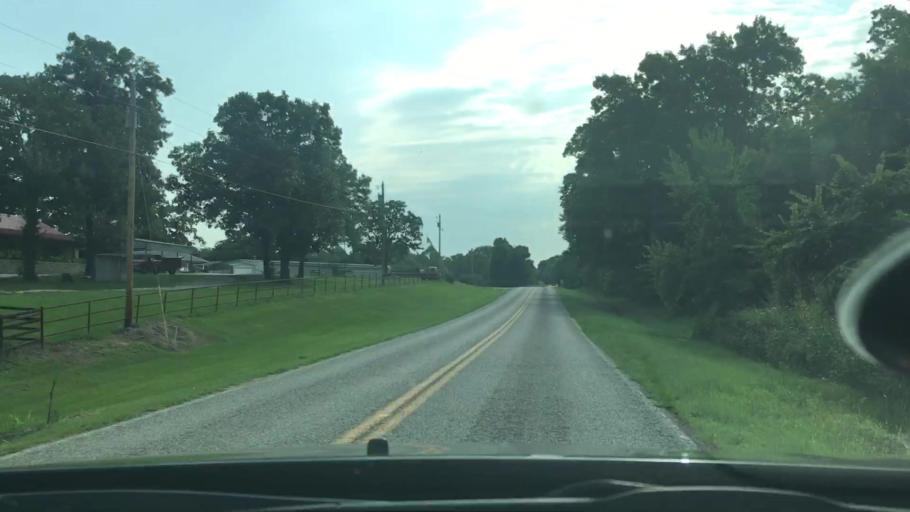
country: US
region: Oklahoma
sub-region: Johnston County
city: Tishomingo
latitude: 34.2087
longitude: -96.5897
